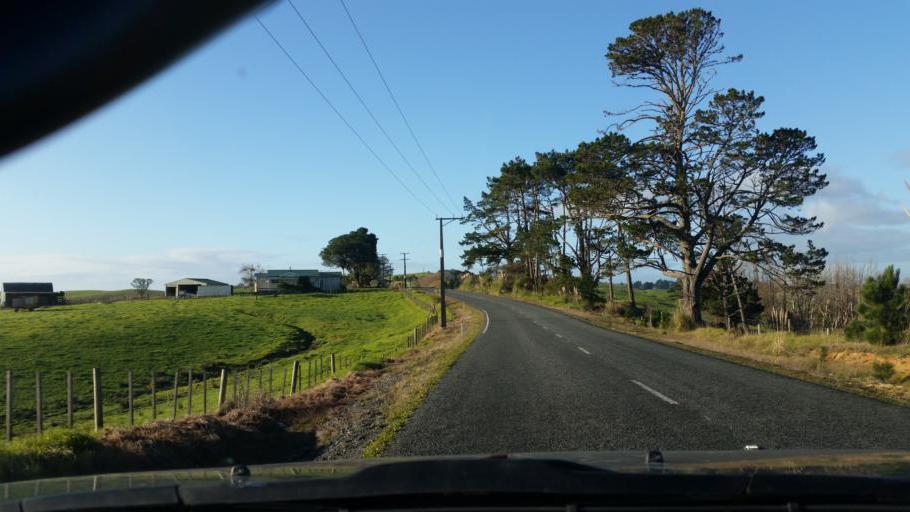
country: NZ
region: Auckland
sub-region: Auckland
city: Wellsford
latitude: -36.1304
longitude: 174.4743
